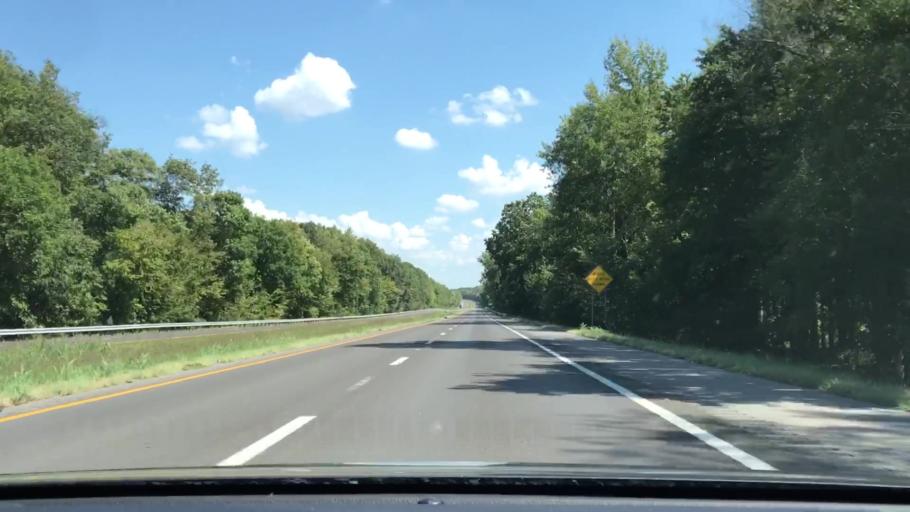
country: US
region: Kentucky
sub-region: Fulton County
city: Fulton
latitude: 36.5931
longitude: -88.8106
